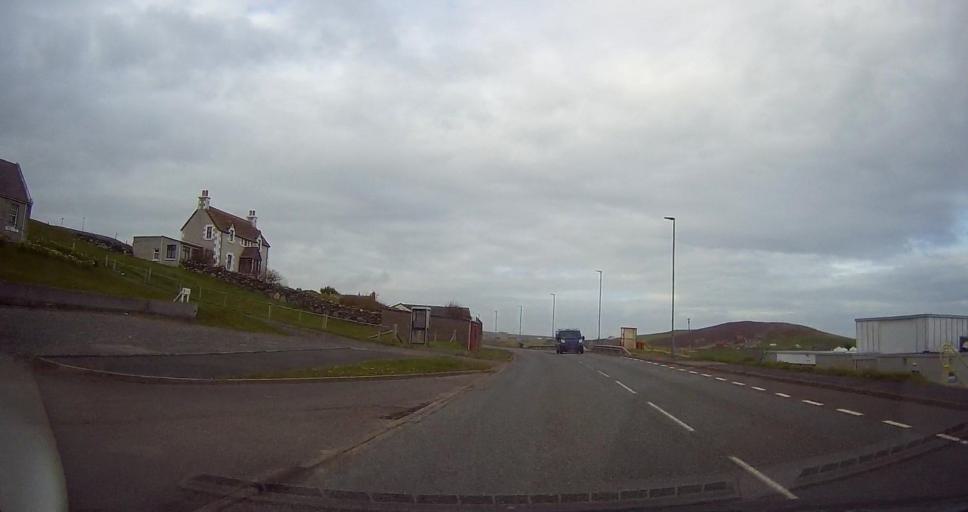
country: GB
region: Scotland
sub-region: Shetland Islands
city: Sandwick
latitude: 60.0451
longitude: -1.2283
